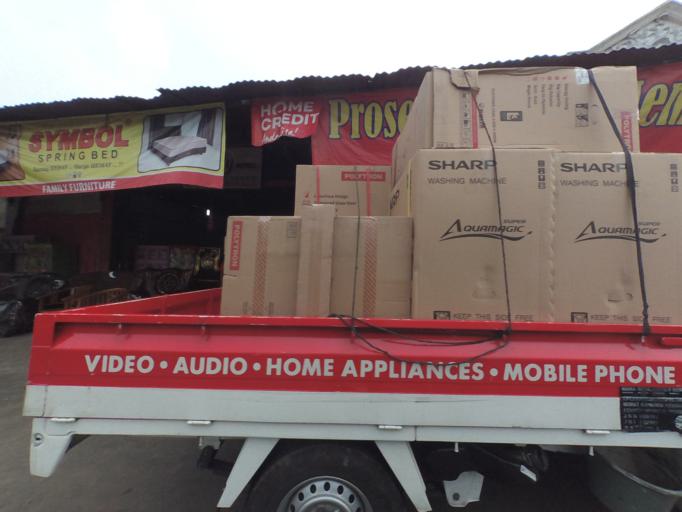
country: ID
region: West Java
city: Ciampea
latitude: -6.5636
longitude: 106.6809
